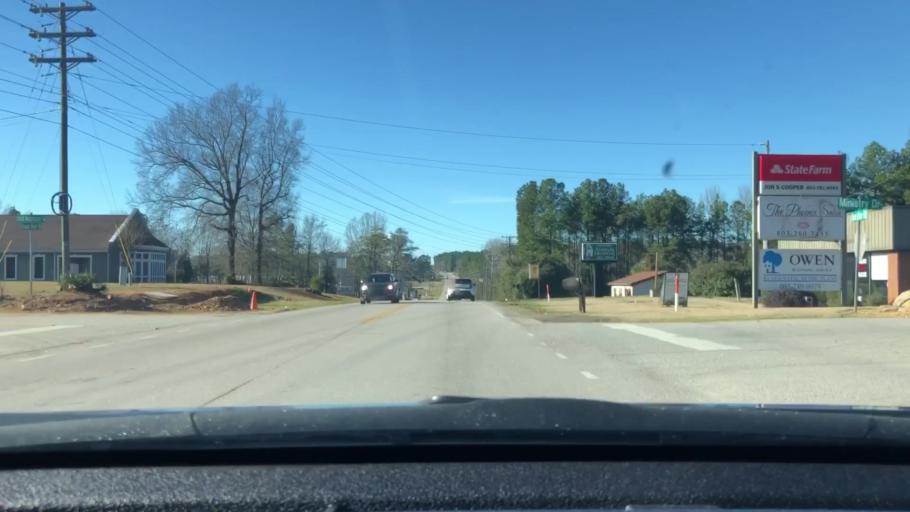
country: US
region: South Carolina
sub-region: Lexington County
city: Irmo
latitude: 34.1145
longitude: -81.1966
